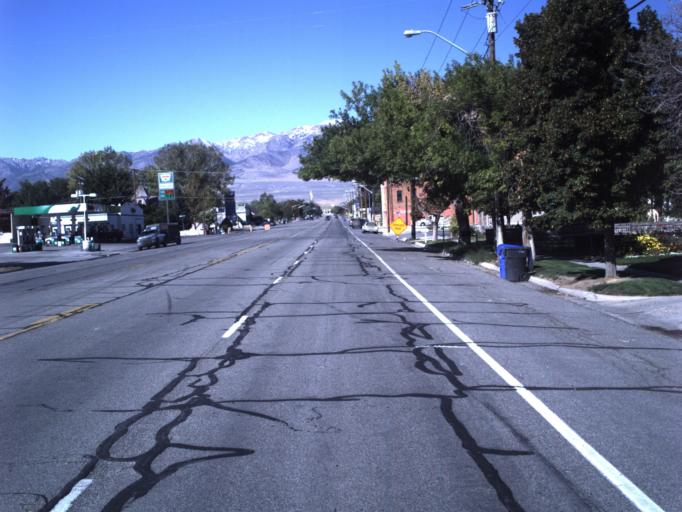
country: US
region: Utah
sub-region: Tooele County
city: Grantsville
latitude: 40.5999
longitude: -112.4619
